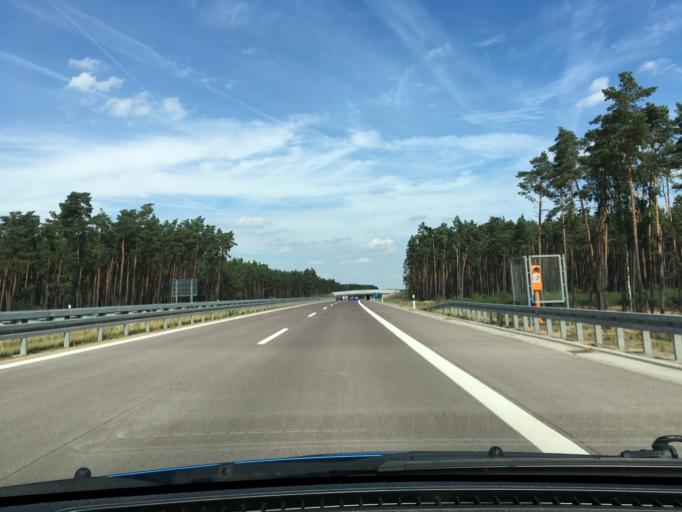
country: DE
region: Mecklenburg-Vorpommern
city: Gross Laasch
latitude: 53.3649
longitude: 11.5164
